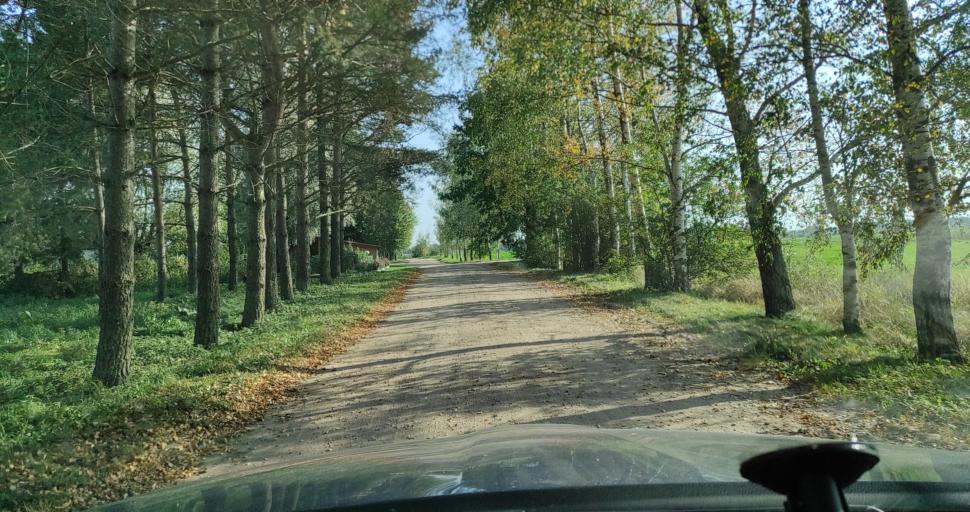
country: LV
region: Ventspils Rajons
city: Piltene
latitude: 57.2238
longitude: 21.6304
